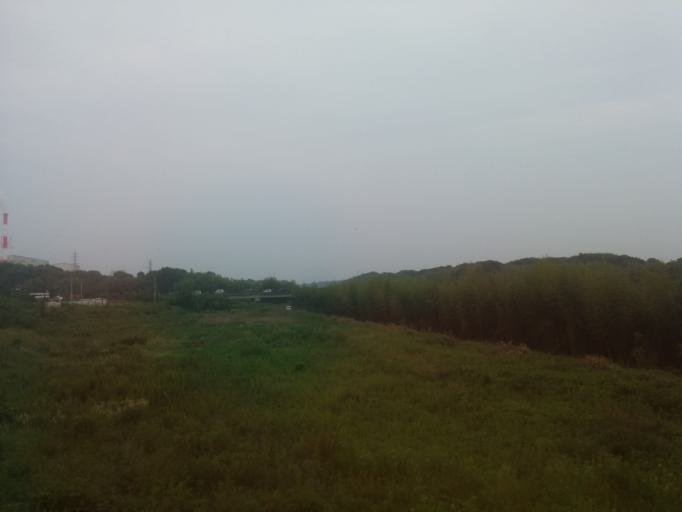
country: JP
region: Shiga Prefecture
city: Youkaichi
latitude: 35.1927
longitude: 136.1804
